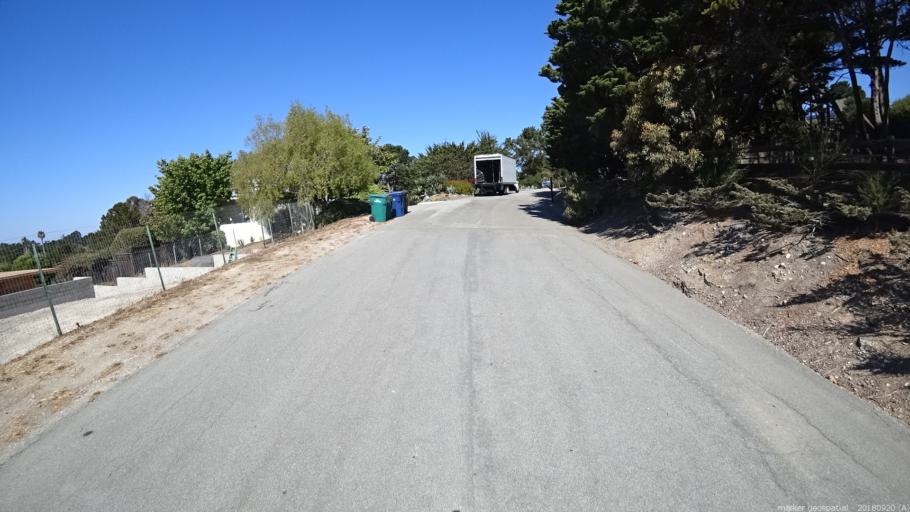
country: US
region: California
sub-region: Monterey County
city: Carmel-by-the-Sea
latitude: 36.5474
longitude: -121.9026
